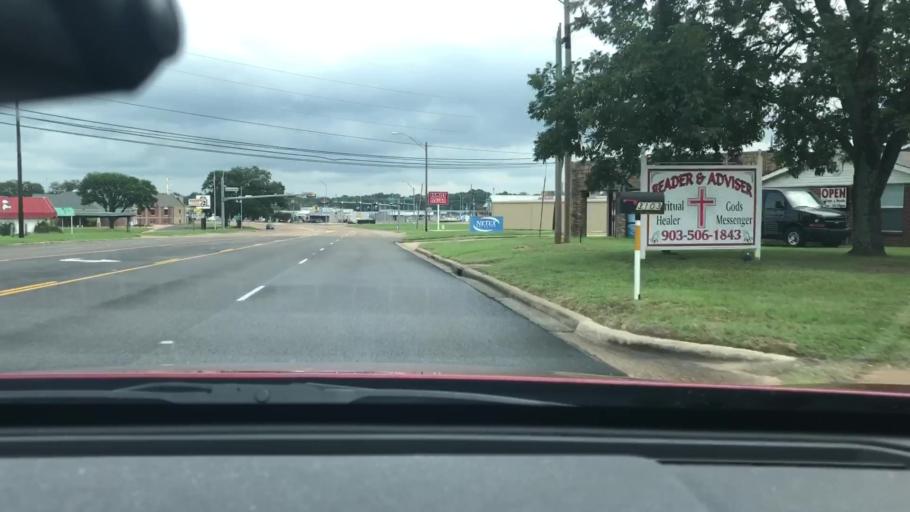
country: US
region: Texas
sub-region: Bowie County
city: Wake Village
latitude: 33.4377
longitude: -94.0840
